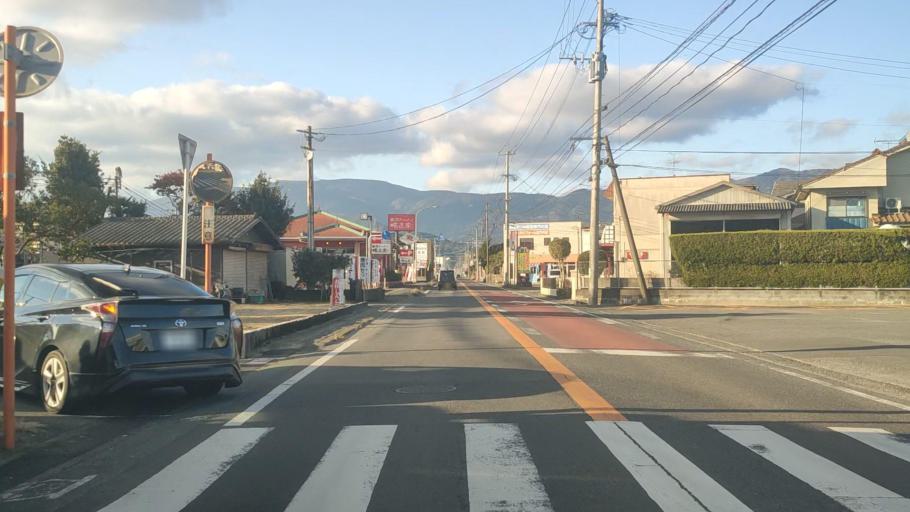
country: JP
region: Saga Prefecture
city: Saga-shi
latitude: 33.2815
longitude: 130.2117
